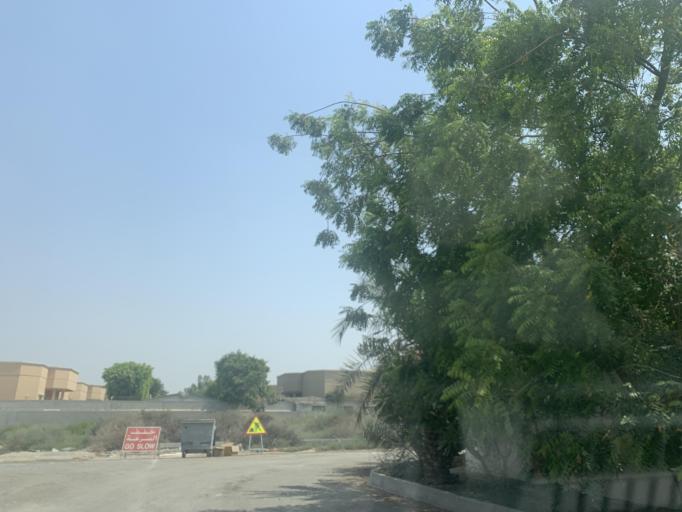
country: BH
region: Manama
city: Jidd Hafs
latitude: 26.1999
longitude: 50.4909
